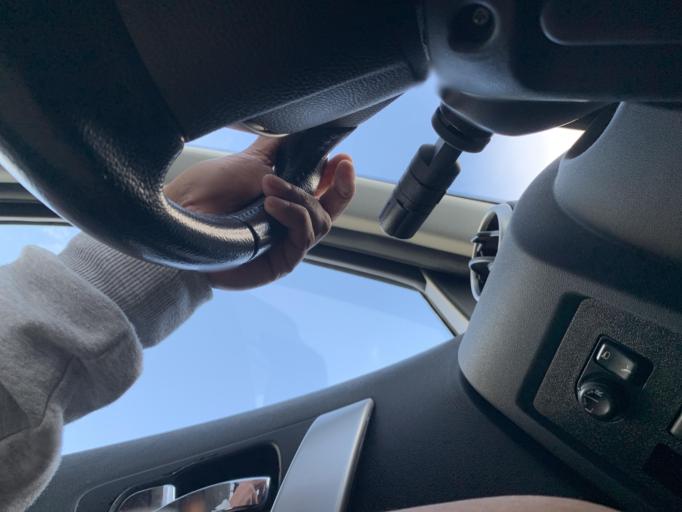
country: NO
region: Rogaland
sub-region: Bjerkreim
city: Vikesa
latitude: 58.5235
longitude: 6.0938
